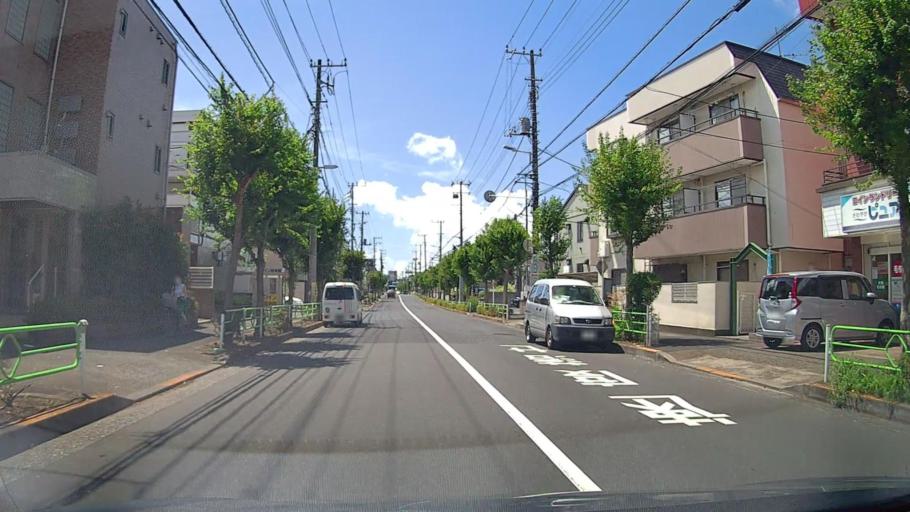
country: JP
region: Tokyo
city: Nishi-Tokyo-shi
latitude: 35.7404
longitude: 139.5659
